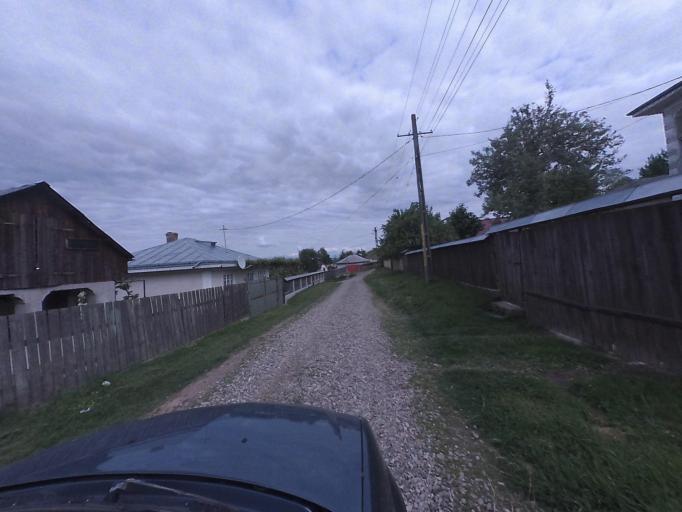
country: RO
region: Neamt
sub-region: Comuna Dulcesti
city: Dulcesti
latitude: 46.9607
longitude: 26.7831
